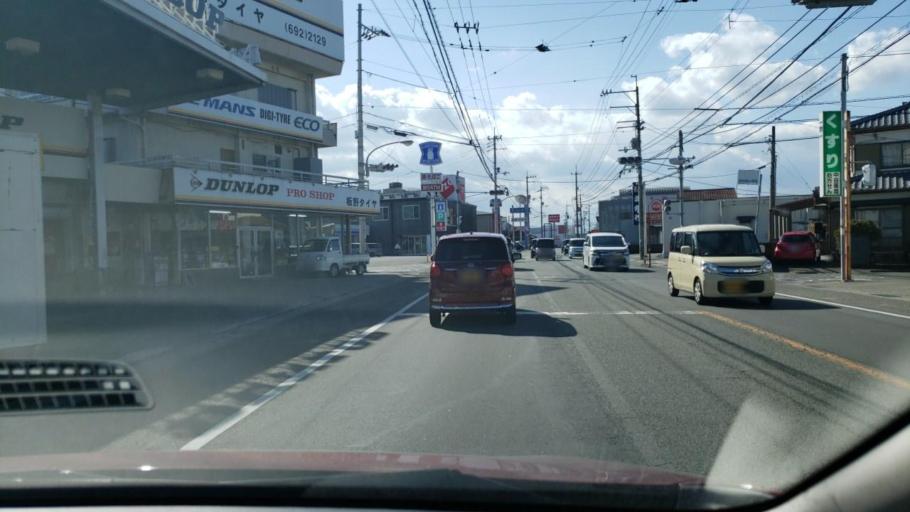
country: JP
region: Tokushima
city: Ishii
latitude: 34.1310
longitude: 134.4860
